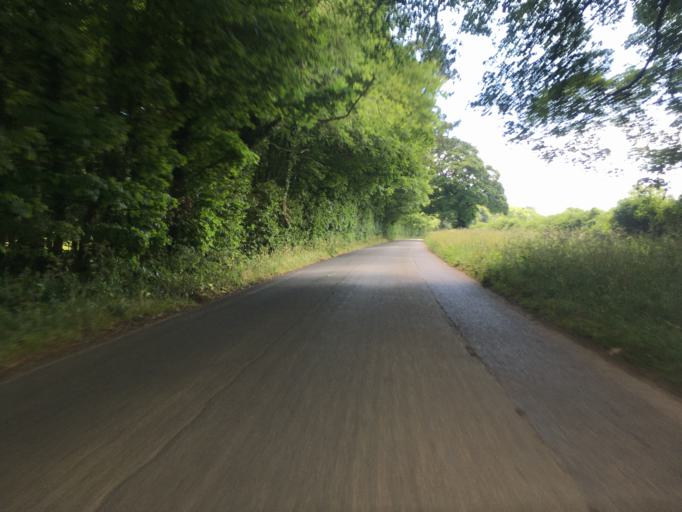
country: GB
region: England
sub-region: Gloucestershire
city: Coates
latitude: 51.7293
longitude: -2.0632
